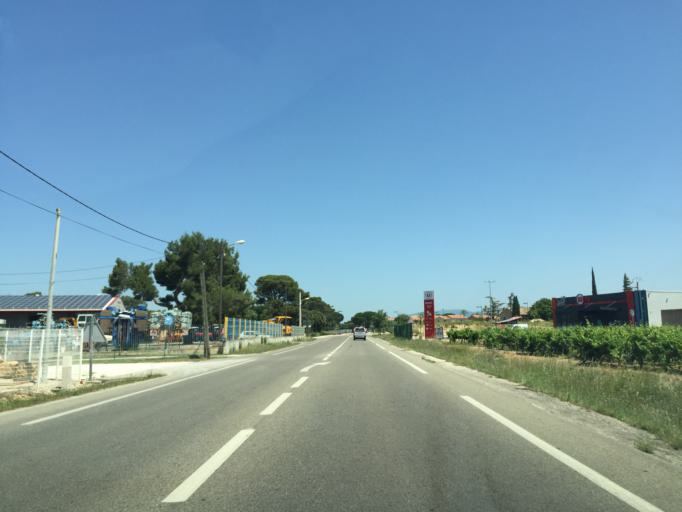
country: FR
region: Provence-Alpes-Cote d'Azur
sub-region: Departement du Vaucluse
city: Sainte-Cecile-les-Vignes
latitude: 44.2317
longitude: 4.8813
